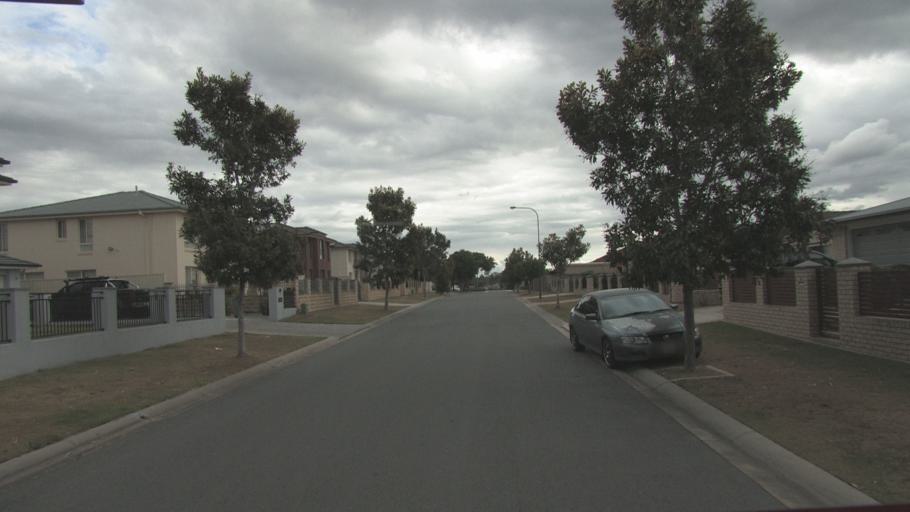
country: AU
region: Queensland
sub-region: Logan
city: Park Ridge South
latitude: -27.6822
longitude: 153.0456
